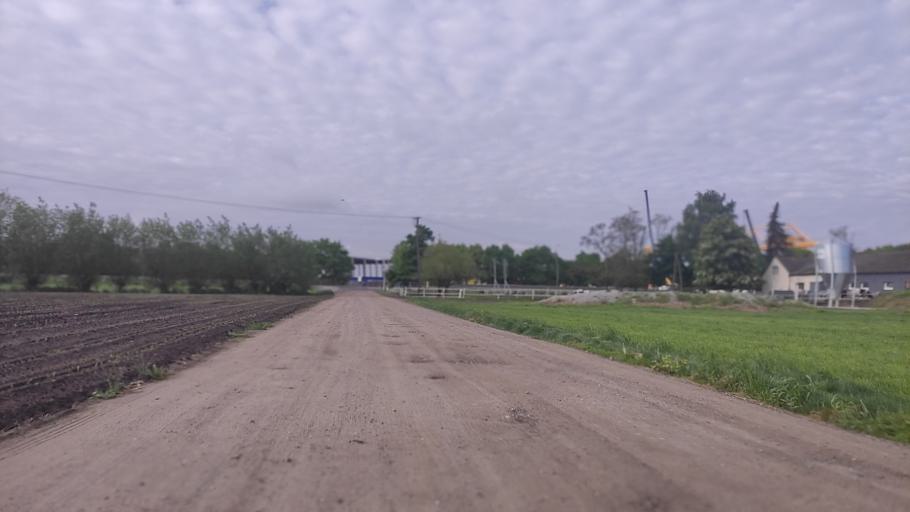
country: PL
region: Greater Poland Voivodeship
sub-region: Powiat poznanski
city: Swarzedz
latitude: 52.4008
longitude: 17.1386
